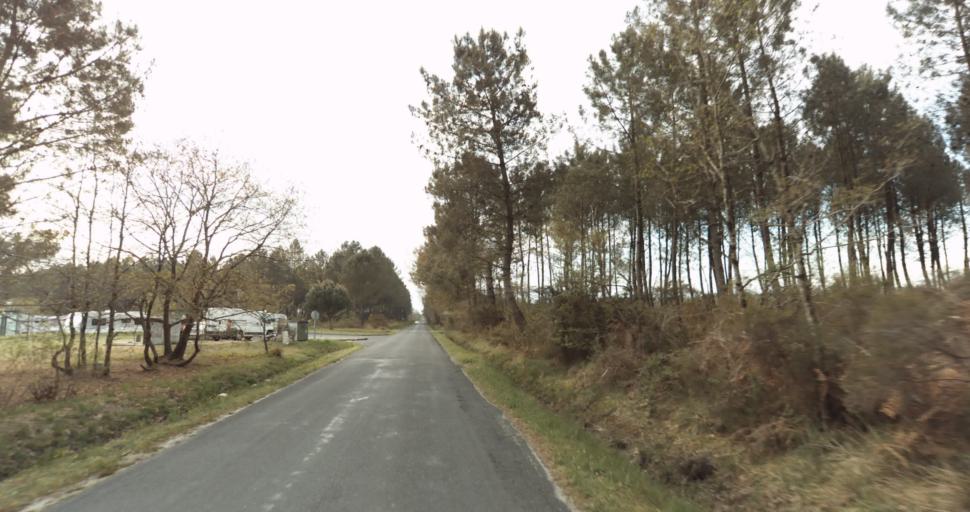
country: FR
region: Aquitaine
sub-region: Departement de la Gironde
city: Martignas-sur-Jalle
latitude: 44.8020
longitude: -0.7682
